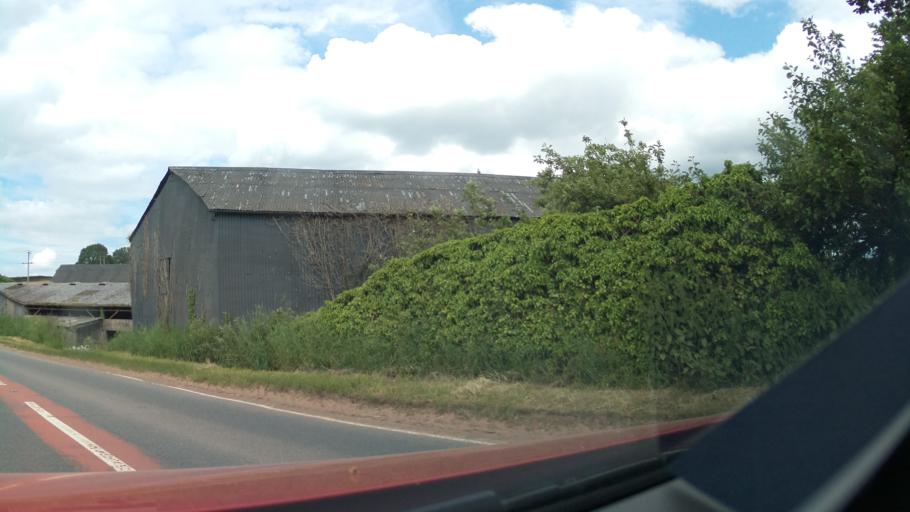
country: GB
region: England
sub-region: Herefordshire
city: Ross on Wye
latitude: 51.9344
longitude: -2.5599
